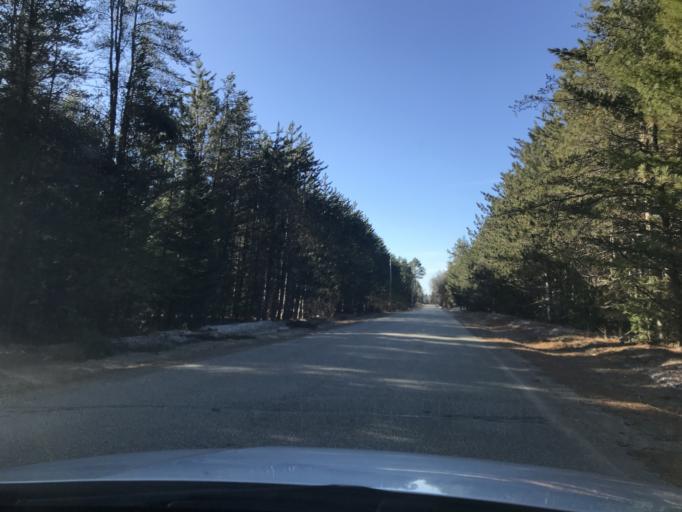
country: US
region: Michigan
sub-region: Dickinson County
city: Kingsford
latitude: 45.3952
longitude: -88.1612
